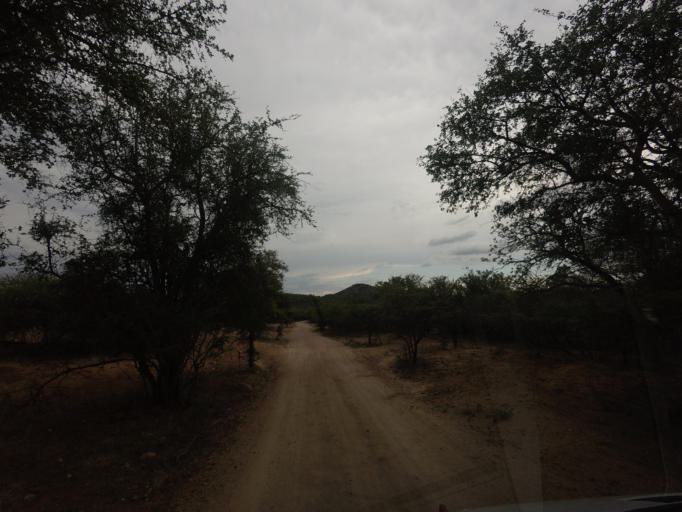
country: ZA
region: Limpopo
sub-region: Mopani District Municipality
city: Hoedspruit
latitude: -24.5104
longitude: 30.9036
